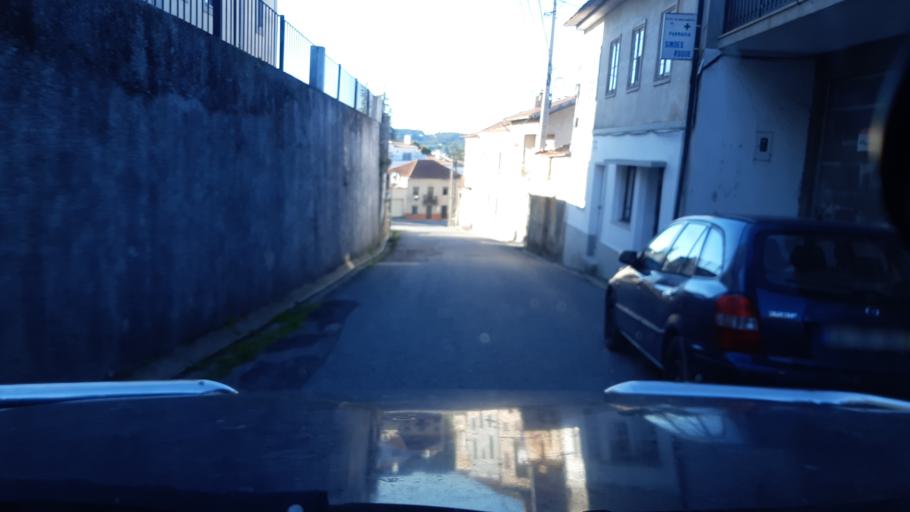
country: PT
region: Aveiro
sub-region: Agueda
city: Agueda
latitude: 40.5587
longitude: -8.4381
